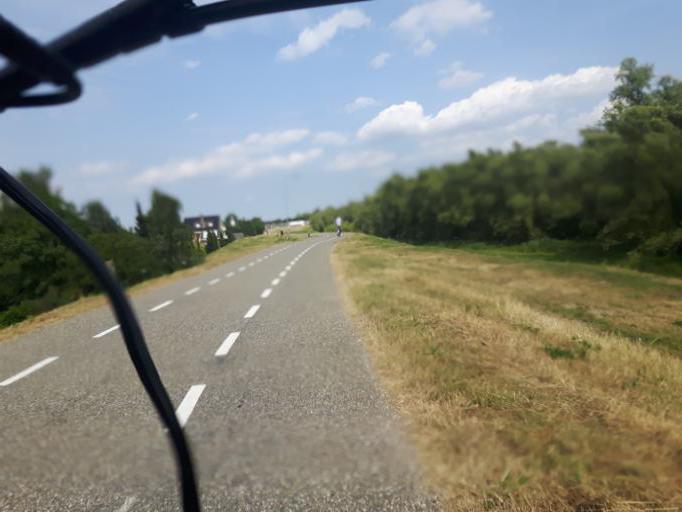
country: NL
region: Gelderland
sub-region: Gemeente Zaltbommel
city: Zaltbommel
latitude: 51.8238
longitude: 5.2508
